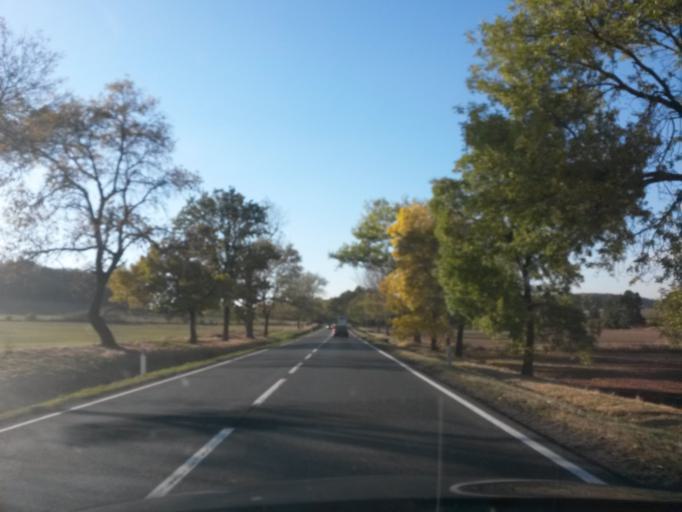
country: PL
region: Lower Silesian Voivodeship
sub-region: Powiat jaworski
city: Bolkow
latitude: 50.9157
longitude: 16.1268
